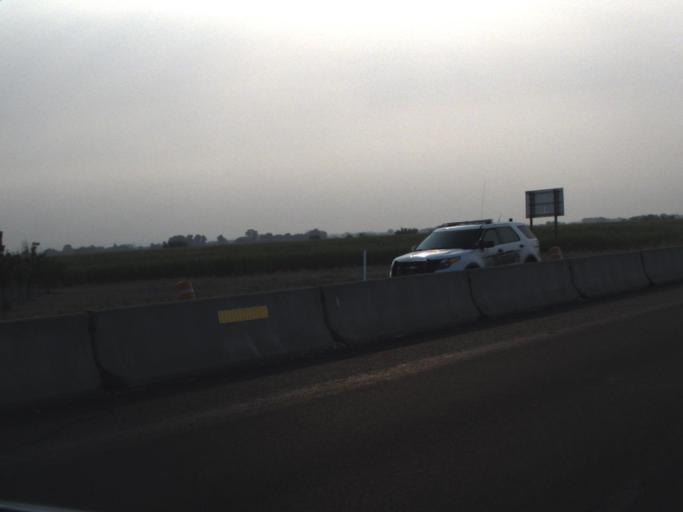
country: US
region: Washington
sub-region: Yakima County
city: Wapato
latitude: 46.4312
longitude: -120.4157
